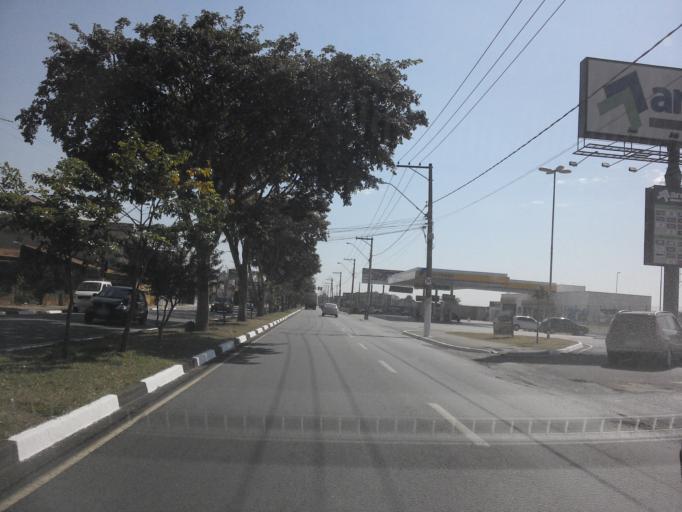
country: BR
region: Sao Paulo
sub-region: Hortolandia
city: Hortolandia
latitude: -22.8925
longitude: -47.2304
